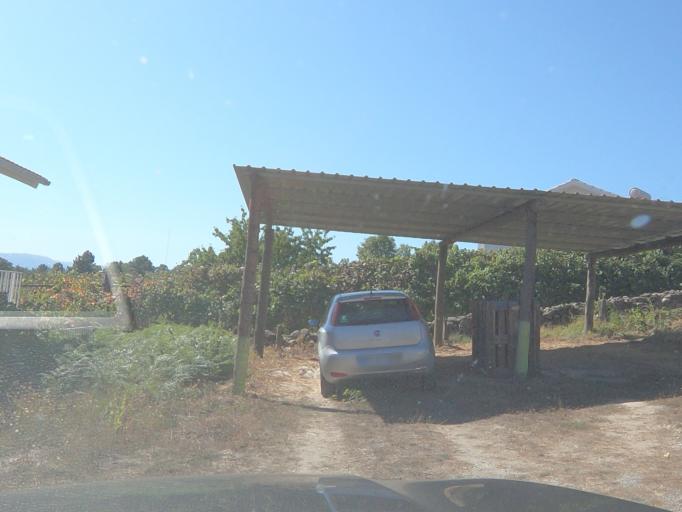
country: PT
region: Vila Real
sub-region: Vila Real
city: Vila Real
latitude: 41.3181
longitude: -7.7251
